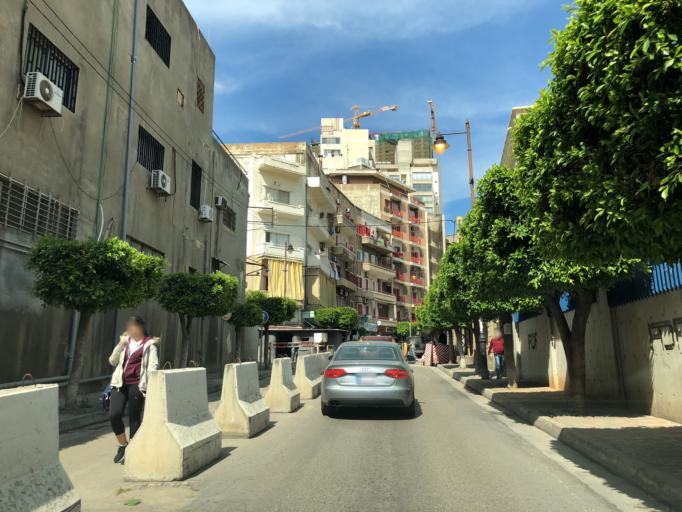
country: LB
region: Beyrouth
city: Beirut
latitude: 33.8812
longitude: 35.5176
